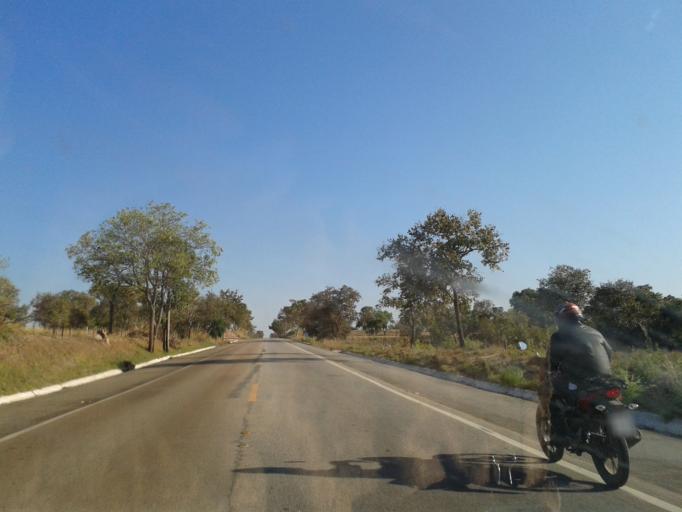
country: BR
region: Goias
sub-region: Mozarlandia
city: Mozarlandia
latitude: -15.2667
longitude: -50.4871
